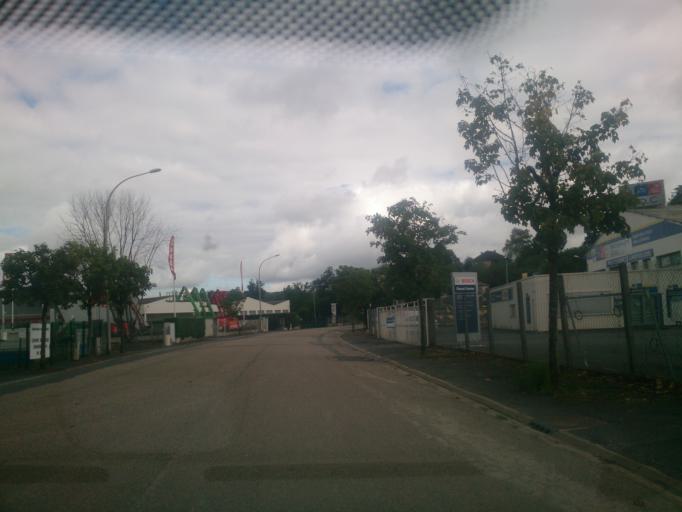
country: FR
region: Limousin
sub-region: Departement de la Correze
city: Saint-Pantaleon-de-Larche
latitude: 45.1605
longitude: 1.4819
